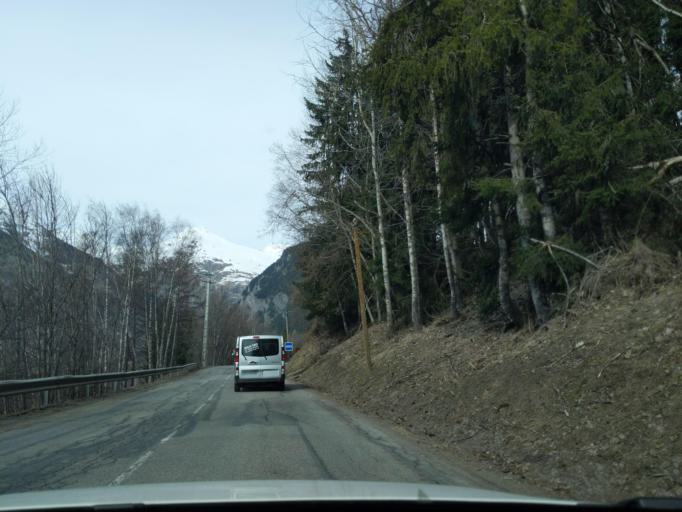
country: FR
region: Rhone-Alpes
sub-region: Departement de la Savoie
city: Bourg-Saint-Maurice
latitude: 45.6075
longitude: 6.7852
